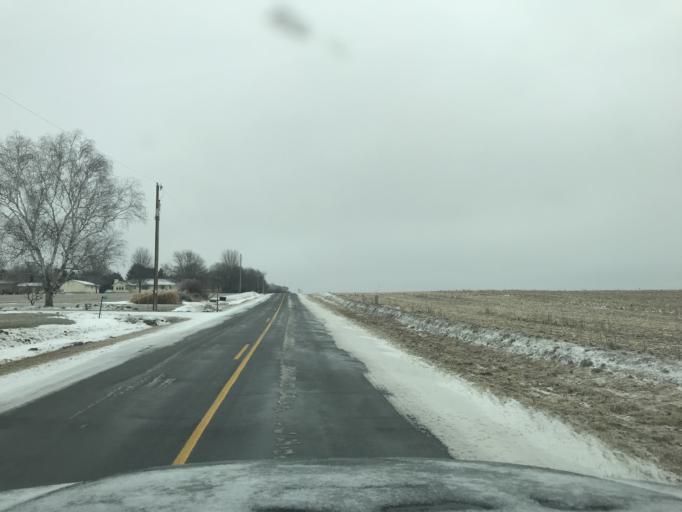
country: US
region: Wisconsin
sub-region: Dane County
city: Cottage Grove
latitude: 43.1040
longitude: -89.2337
